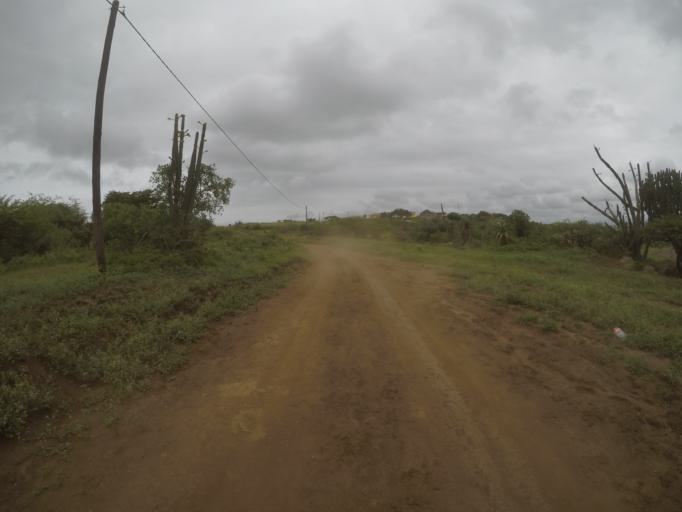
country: ZA
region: KwaZulu-Natal
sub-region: uThungulu District Municipality
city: Empangeni
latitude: -28.6020
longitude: 31.8459
